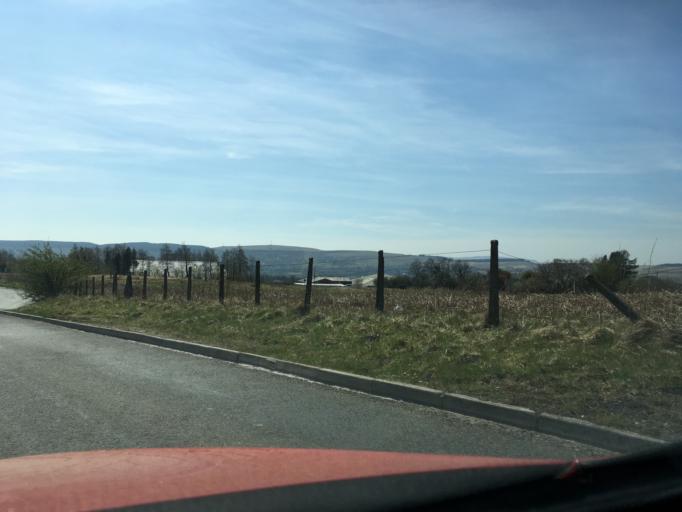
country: GB
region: Wales
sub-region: Merthyr Tydfil County Borough
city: Merthyr Tydfil
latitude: 51.7690
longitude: -3.3692
